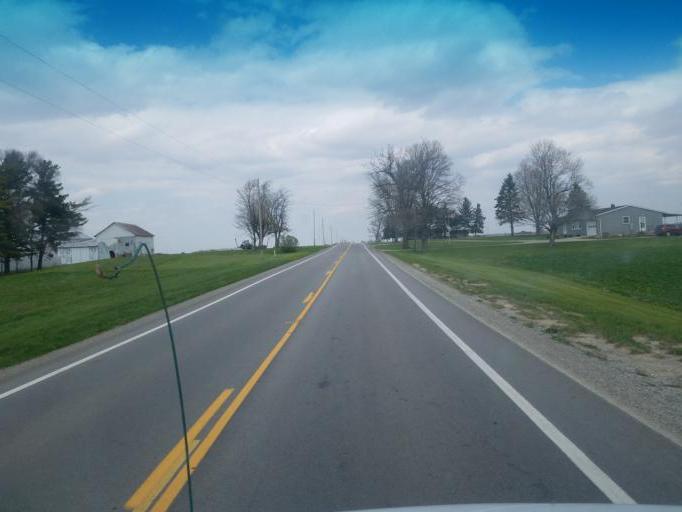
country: US
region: Ohio
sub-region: Wyandot County
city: Upper Sandusky
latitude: 40.8850
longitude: -83.2769
